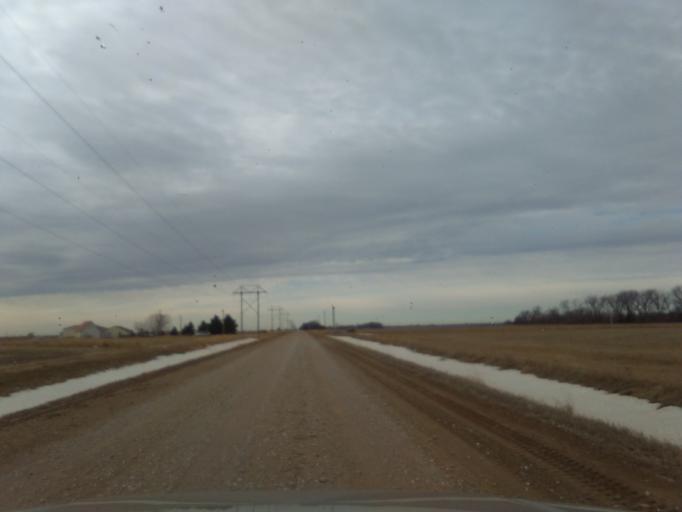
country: US
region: Nebraska
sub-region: Buffalo County
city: Gibbon
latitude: 40.6550
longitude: -98.7889
